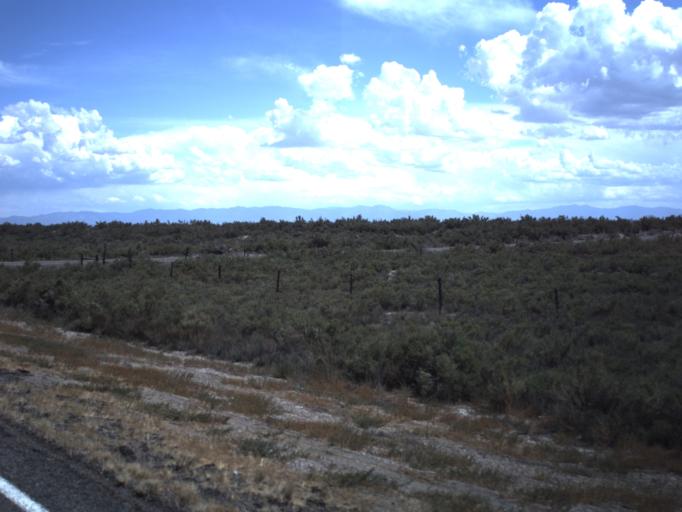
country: US
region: Utah
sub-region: Millard County
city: Delta
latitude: 39.3309
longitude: -112.7093
